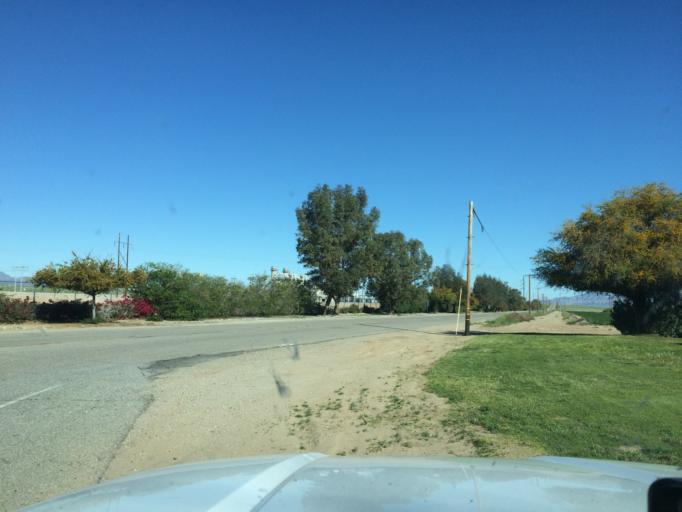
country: US
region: California
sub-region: Riverside County
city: Mesa Verde
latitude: 33.6102
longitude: -114.6835
